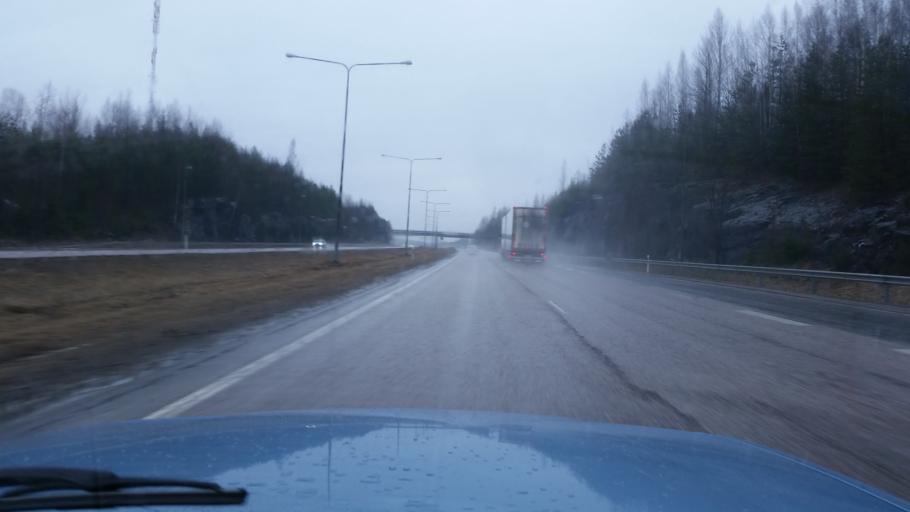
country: FI
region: Uusimaa
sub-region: Helsinki
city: Hyvinge
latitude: 60.5686
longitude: 24.8172
